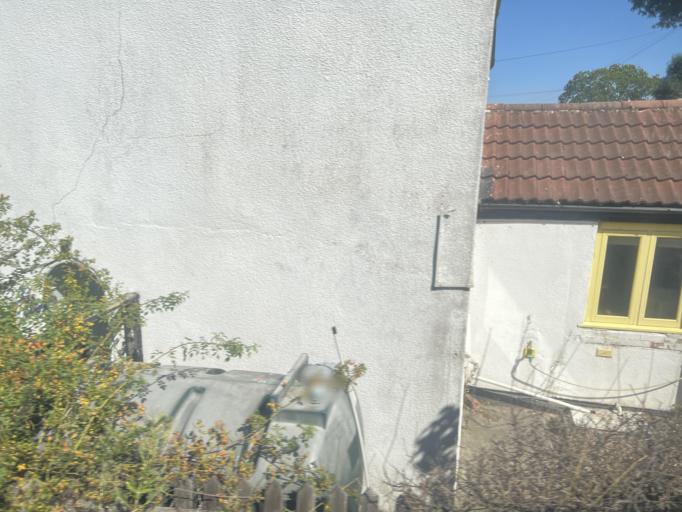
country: GB
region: England
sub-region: Lincolnshire
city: Donington
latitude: 52.9696
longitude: -0.1878
